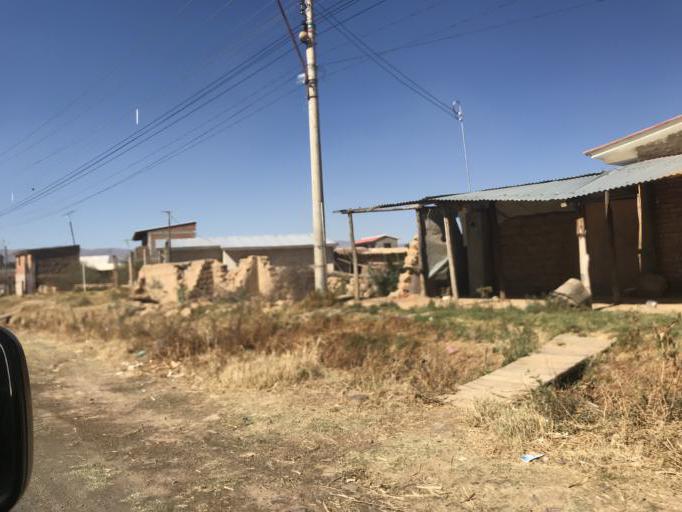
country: BO
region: Cochabamba
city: Cliza
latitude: -17.5736
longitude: -65.9010
